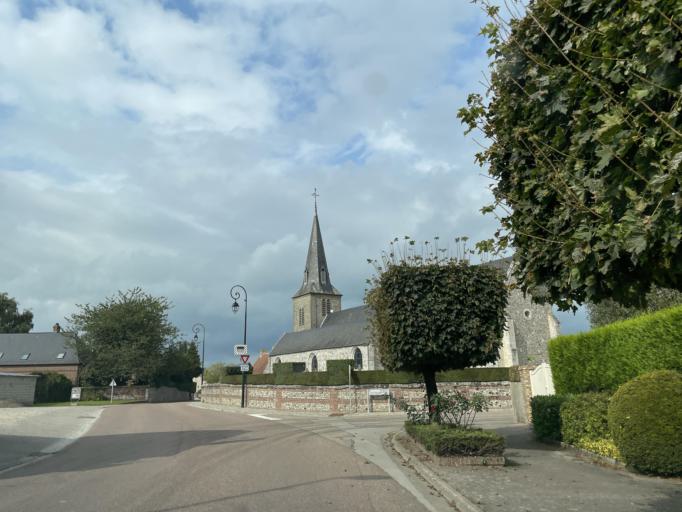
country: FR
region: Haute-Normandie
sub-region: Departement de la Seine-Maritime
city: Saint-Martin-en-Campagne
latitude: 49.9564
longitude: 1.2239
